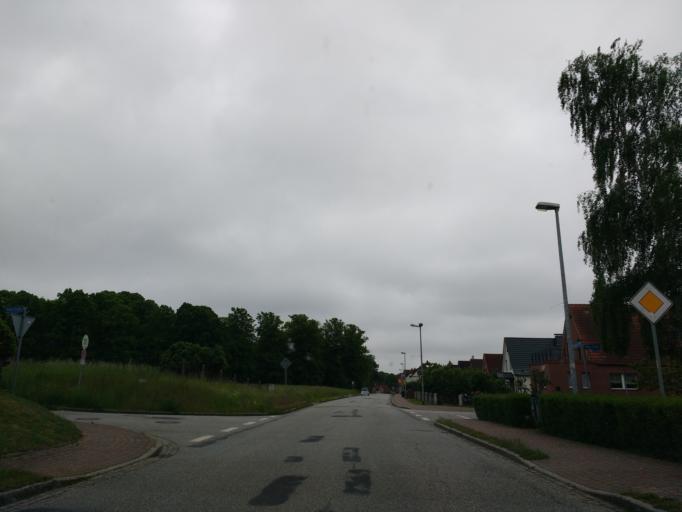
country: DE
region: Mecklenburg-Vorpommern
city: Neukloster
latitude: 53.8688
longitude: 11.6929
